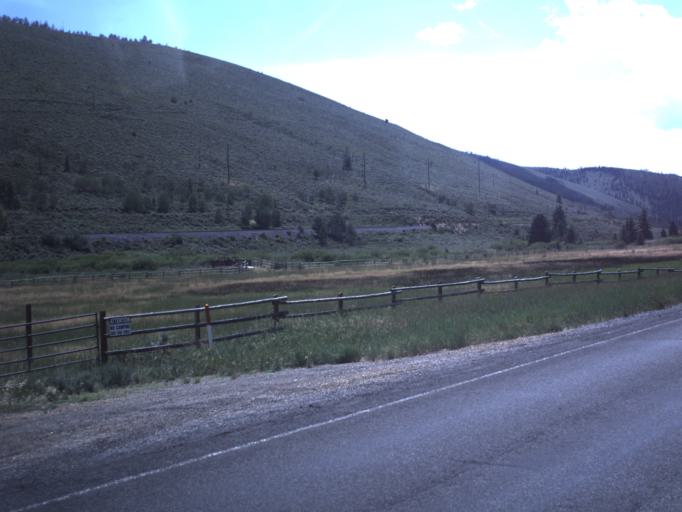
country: US
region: Utah
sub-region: Sanpete County
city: Fairview
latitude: 39.7128
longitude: -111.1633
